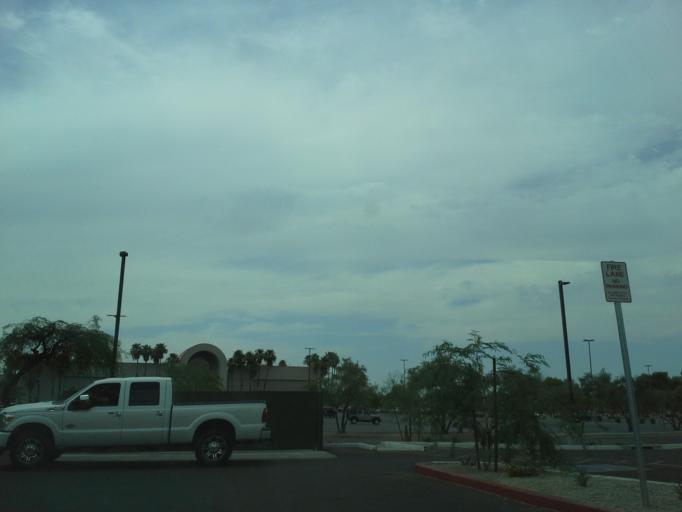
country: US
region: Arizona
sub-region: Maricopa County
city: Paradise Valley
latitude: 33.6031
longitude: -111.9790
